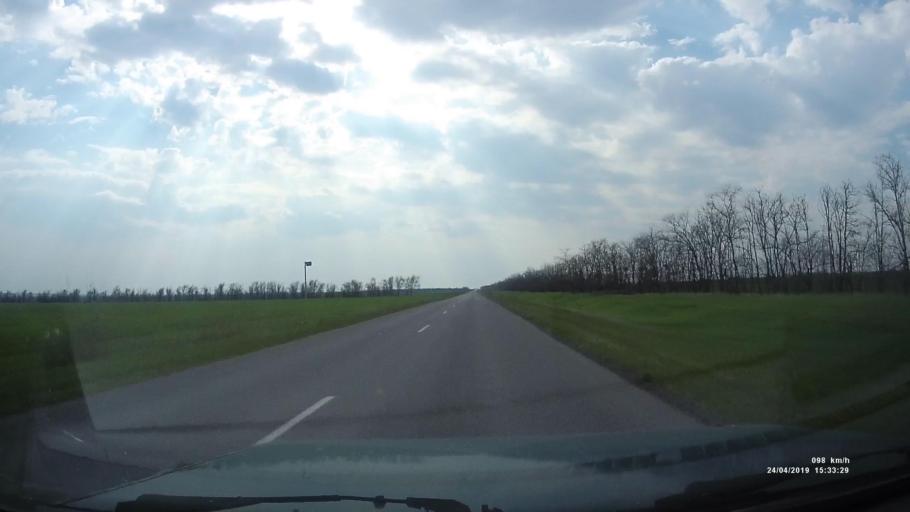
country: RU
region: Kalmykiya
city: Yashalta
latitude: 46.6002
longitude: 42.9373
